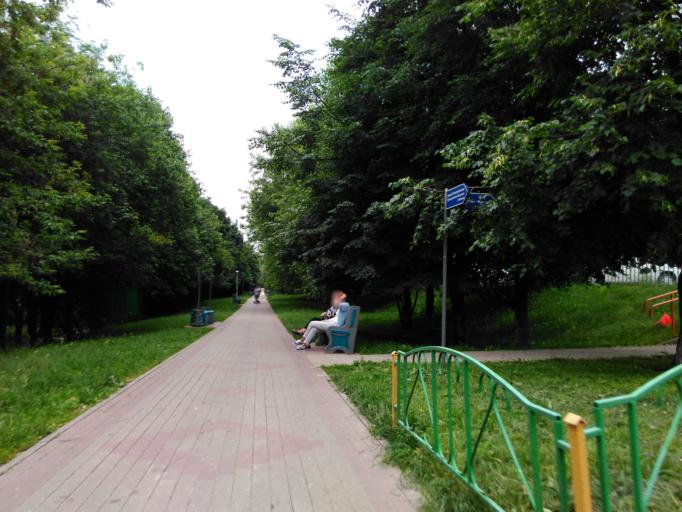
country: RU
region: Moscow
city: Yasenevo
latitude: 55.6305
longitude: 37.5224
